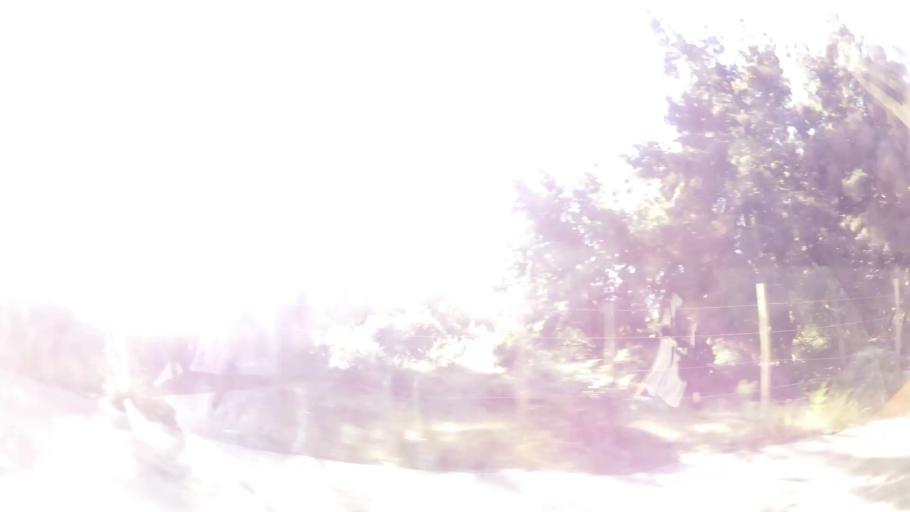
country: CL
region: Valparaiso
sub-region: Provincia de Valparaiso
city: Vina del Mar
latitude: -33.1465
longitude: -71.5613
